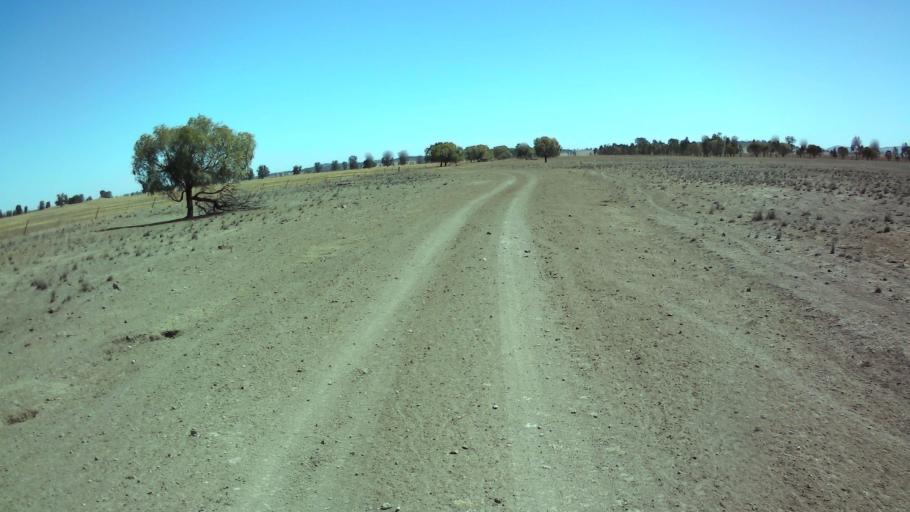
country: AU
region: New South Wales
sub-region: Forbes
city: Forbes
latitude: -33.7215
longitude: 147.6654
